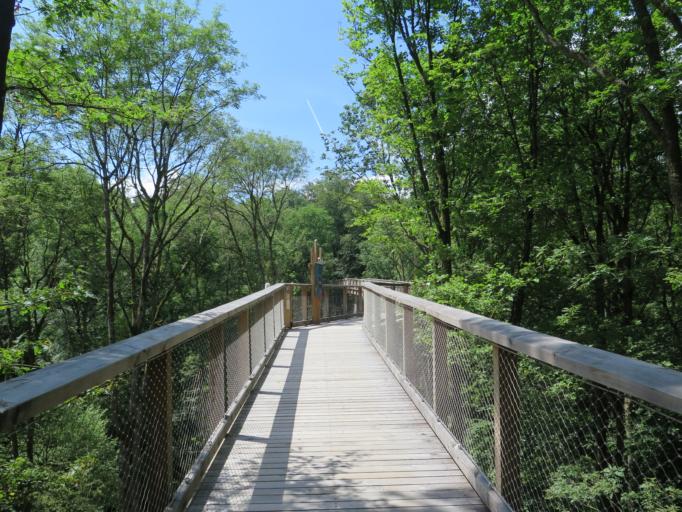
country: DE
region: Bavaria
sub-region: Regierungsbezirk Unterfranken
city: Oberschwarzach
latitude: 49.8502
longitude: 10.4612
